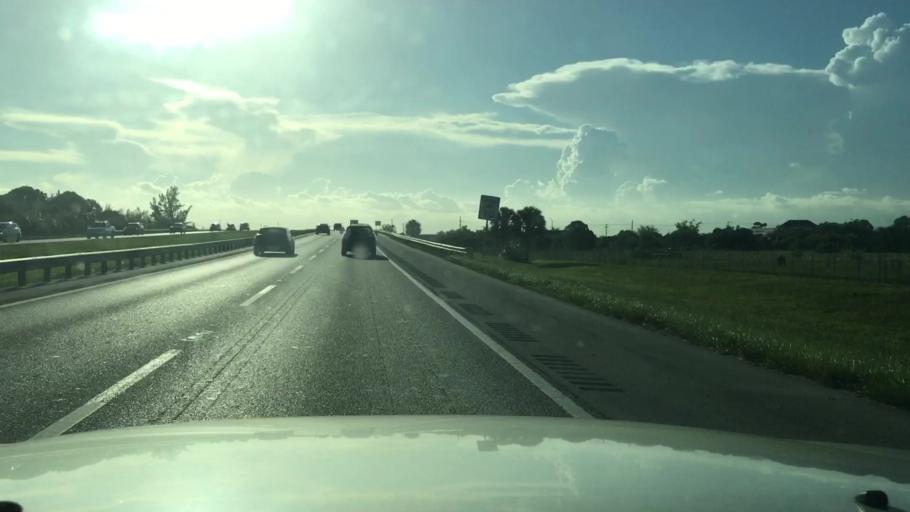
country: US
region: Florida
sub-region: Miami-Dade County
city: Lake Lucerne
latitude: 25.9723
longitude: -80.2589
